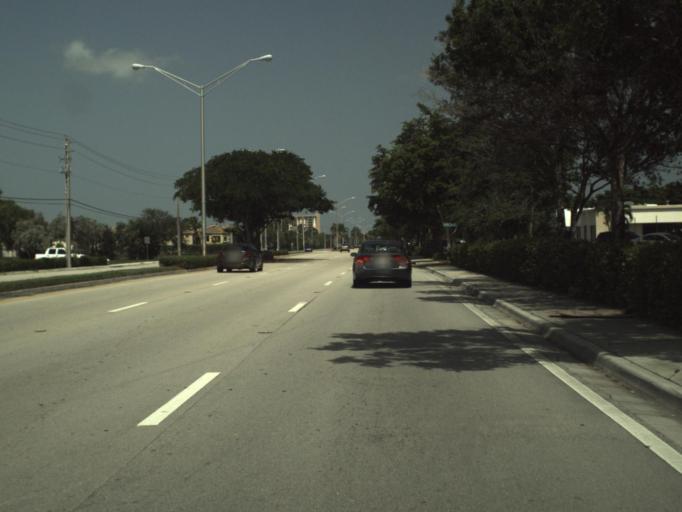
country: US
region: Florida
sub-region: Broward County
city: Coral Springs
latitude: 26.2727
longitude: -80.2800
